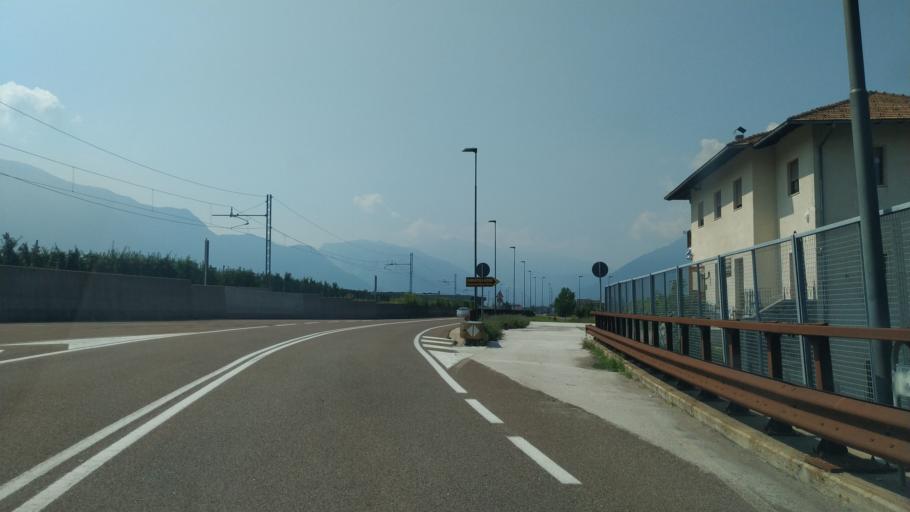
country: IT
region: Trentino-Alto Adige
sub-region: Provincia di Trento
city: Taio
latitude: 46.3032
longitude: 11.0711
